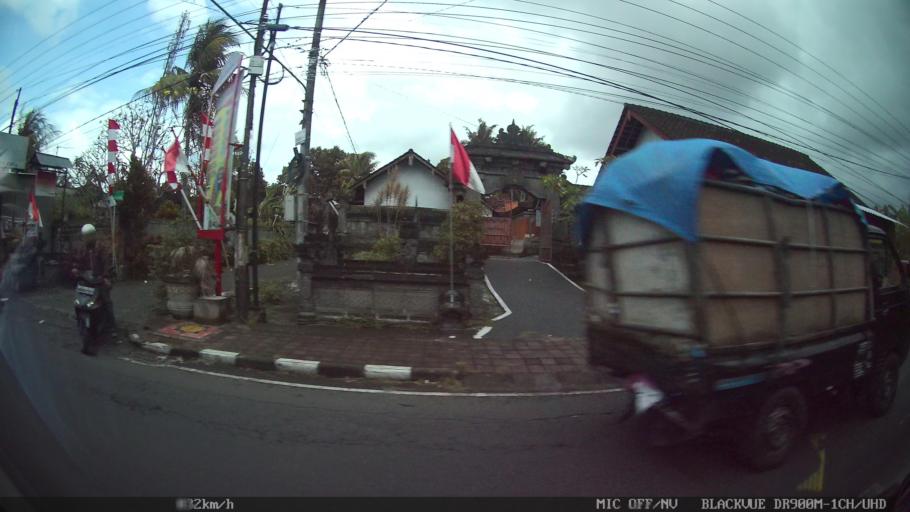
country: ID
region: Bali
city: Banjar Cemenggon
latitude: -8.5382
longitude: 115.1991
